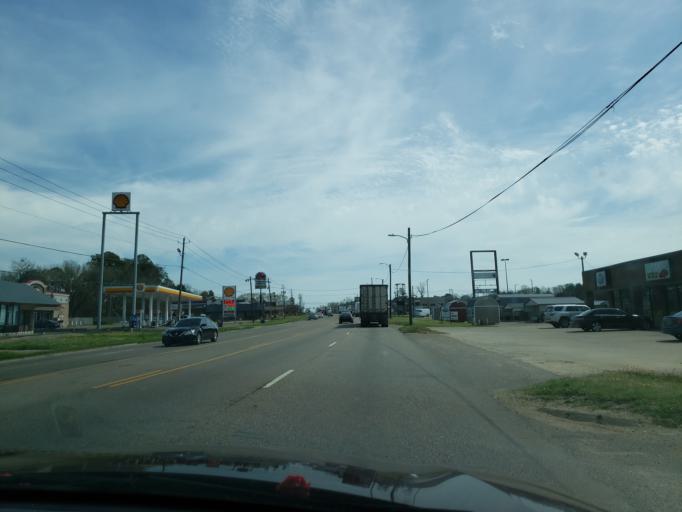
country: US
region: Alabama
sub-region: Dallas County
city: Selma
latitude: 32.4314
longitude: -87.0374
